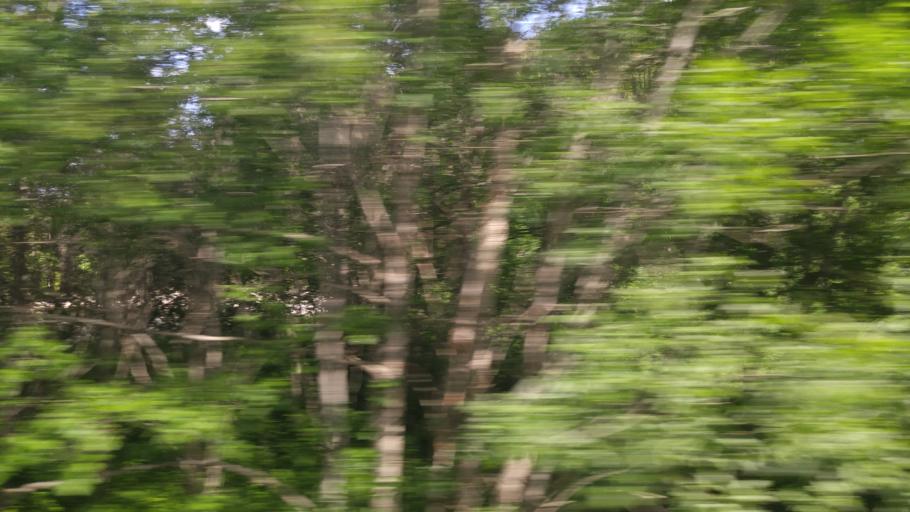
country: NO
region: Sor-Trondelag
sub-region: Klaebu
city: Klaebu
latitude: 62.9508
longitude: 10.6843
